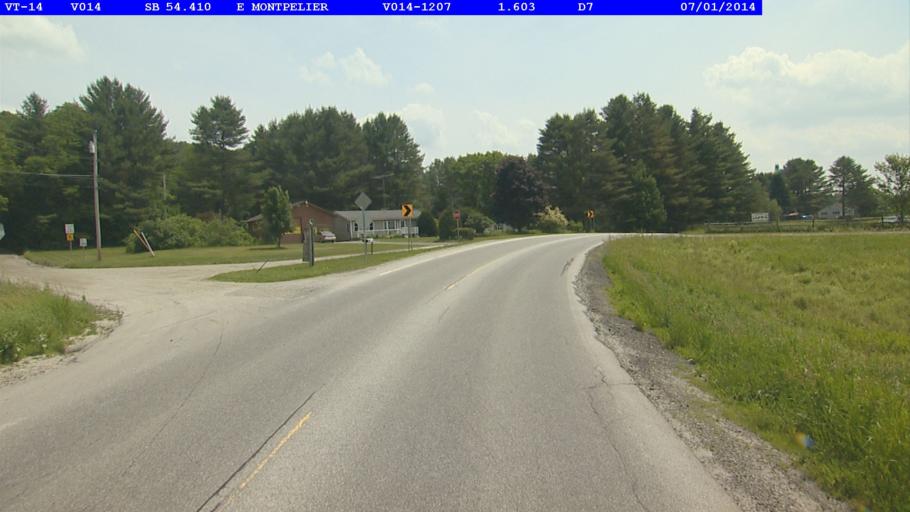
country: US
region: Vermont
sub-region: Washington County
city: Barre
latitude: 44.2576
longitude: -72.4845
